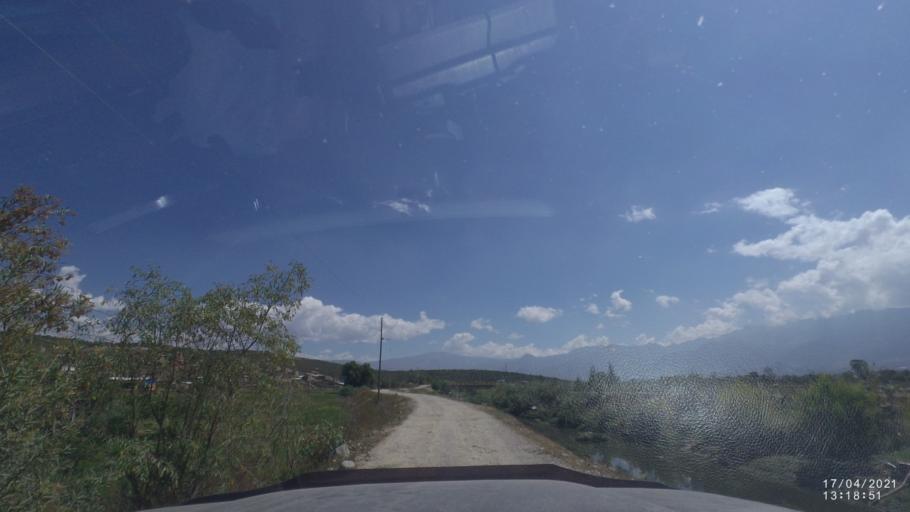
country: BO
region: Cochabamba
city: Cochabamba
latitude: -17.4150
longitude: -66.2451
